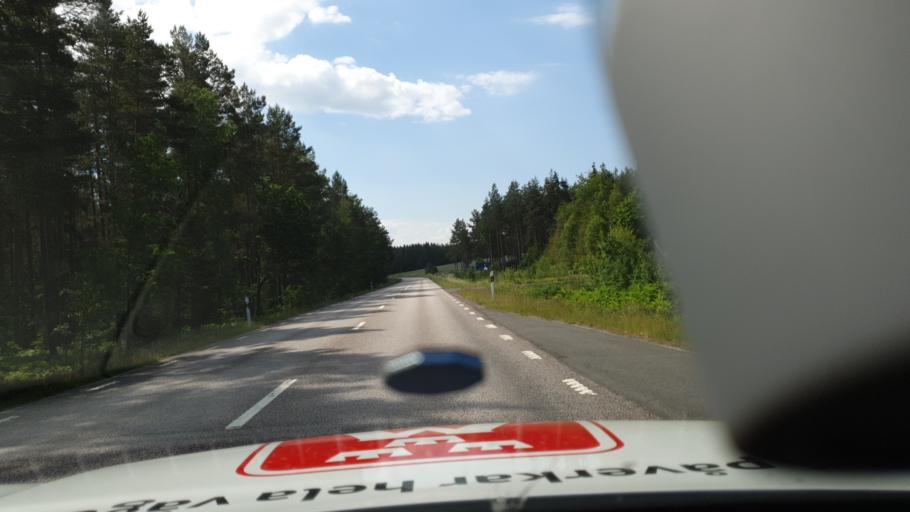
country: SE
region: Vaestra Goetaland
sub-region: Hjo Kommun
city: Hjo
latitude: 58.1917
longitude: 14.2045
